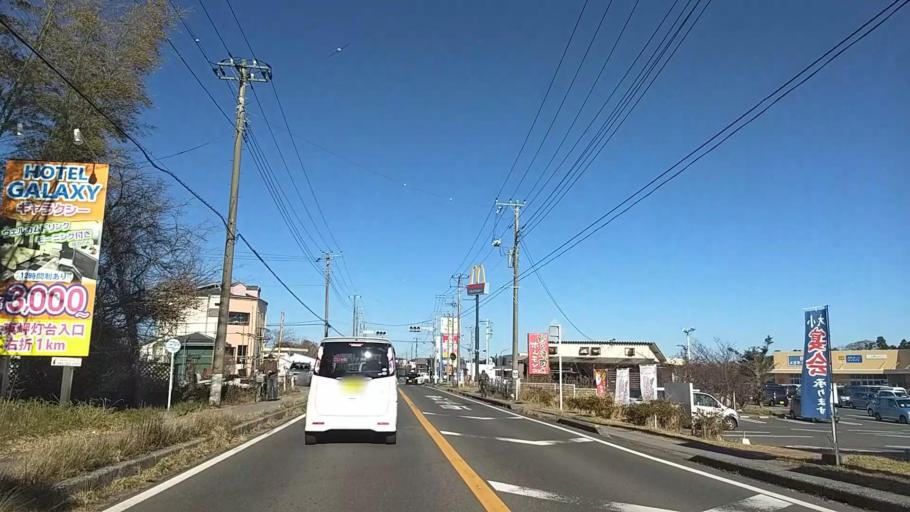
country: JP
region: Chiba
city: Ohara
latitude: 35.2885
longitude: 140.3924
